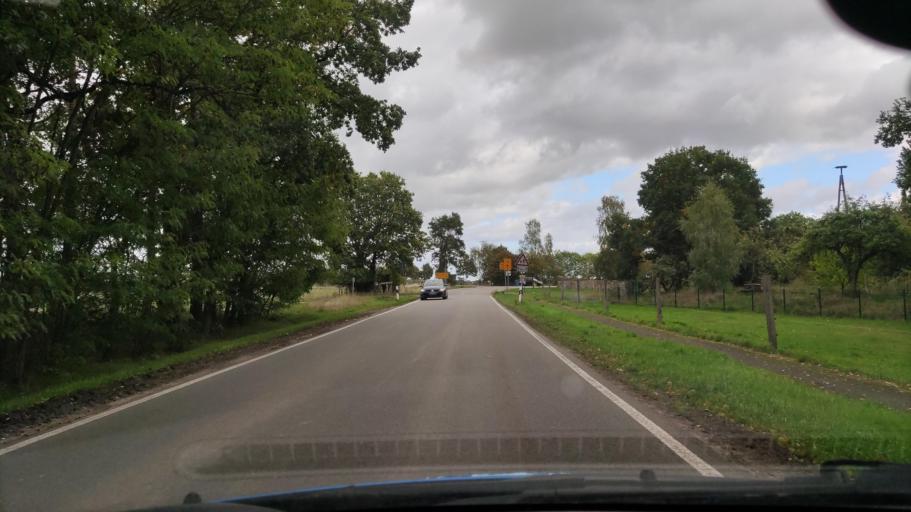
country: DE
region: Saxony-Anhalt
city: Pretzier
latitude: 52.8220
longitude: 11.3774
